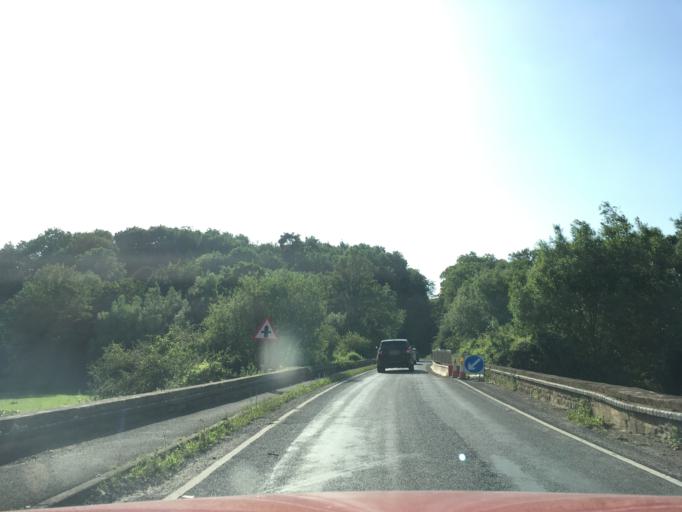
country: GB
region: England
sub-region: Oxfordshire
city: Somerton
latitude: 51.9191
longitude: -1.3045
